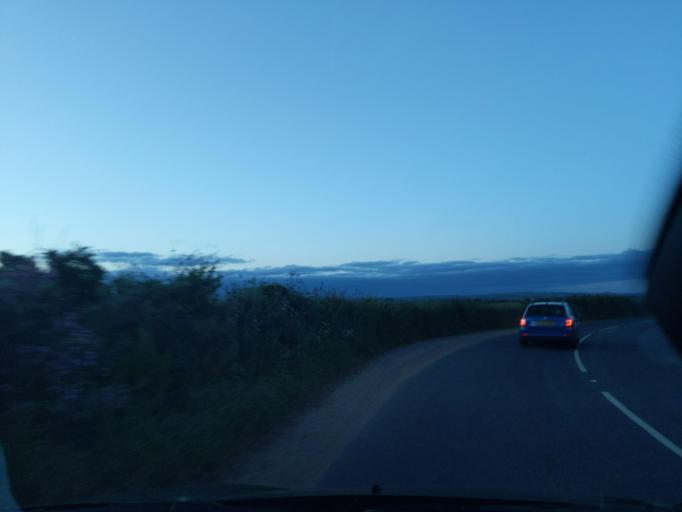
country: GB
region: England
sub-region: Cornwall
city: St. Buryan
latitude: 50.0812
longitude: -5.6167
